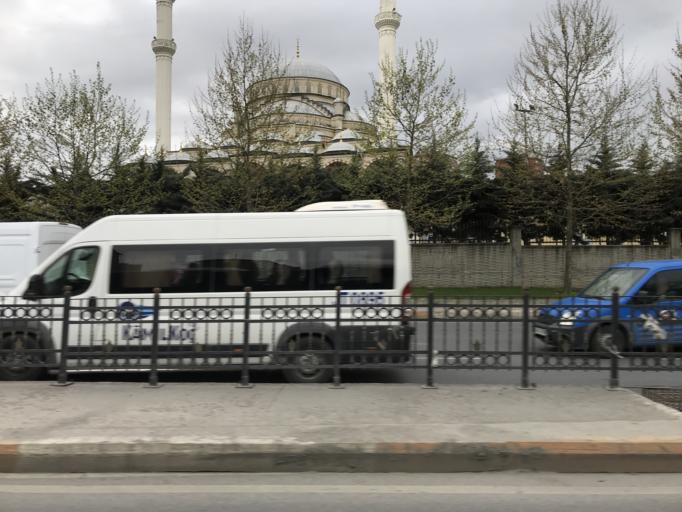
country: TR
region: Istanbul
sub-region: Atasehir
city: Atasehir
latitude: 40.9913
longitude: 29.1509
